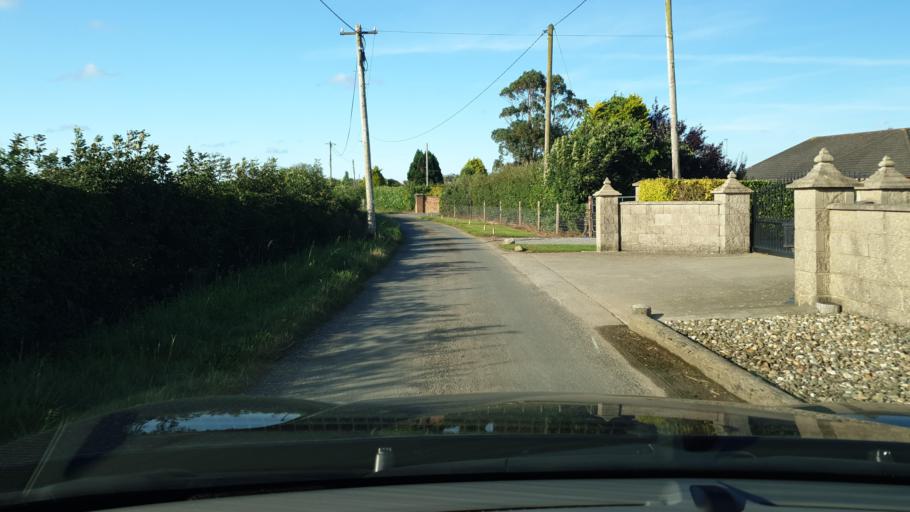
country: IE
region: Leinster
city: Lusk
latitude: 53.5432
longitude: -6.1468
